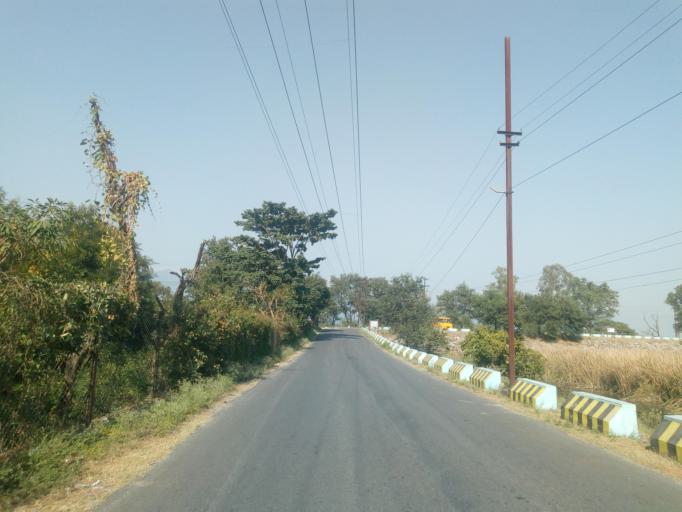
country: IN
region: Himachal Pradesh
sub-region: Sirmaur
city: Paonta Sahib
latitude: 30.4413
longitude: 77.6732
